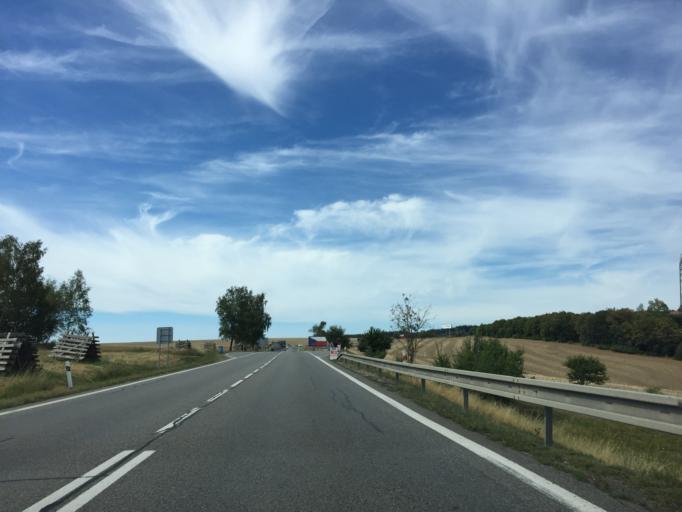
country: CZ
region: Jihocesky
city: Chotoviny
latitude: 49.5566
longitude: 14.6651
